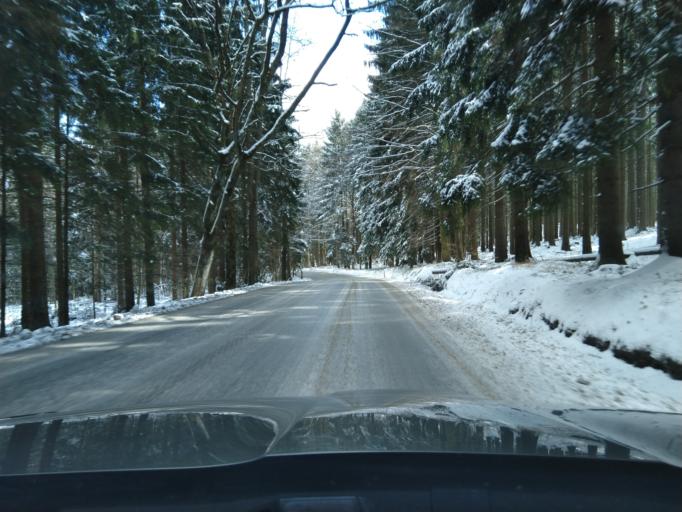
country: CZ
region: Jihocesky
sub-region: Okres Prachatice
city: Zdikov
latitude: 49.0590
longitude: 13.7136
